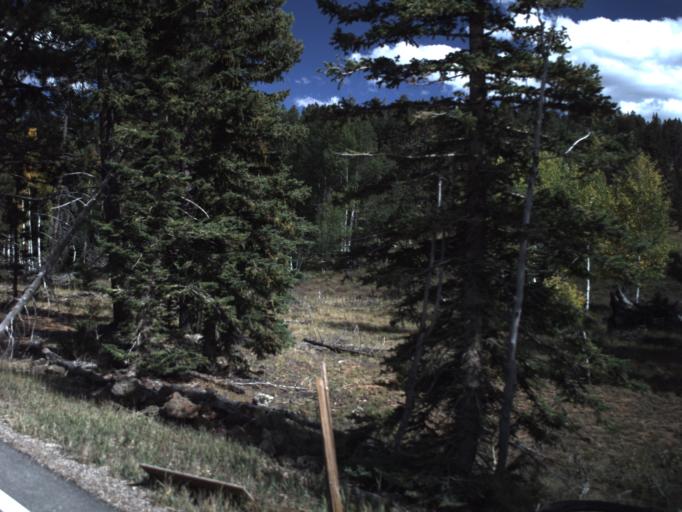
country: US
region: Utah
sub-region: Iron County
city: Parowan
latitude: 37.5194
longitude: -112.6731
